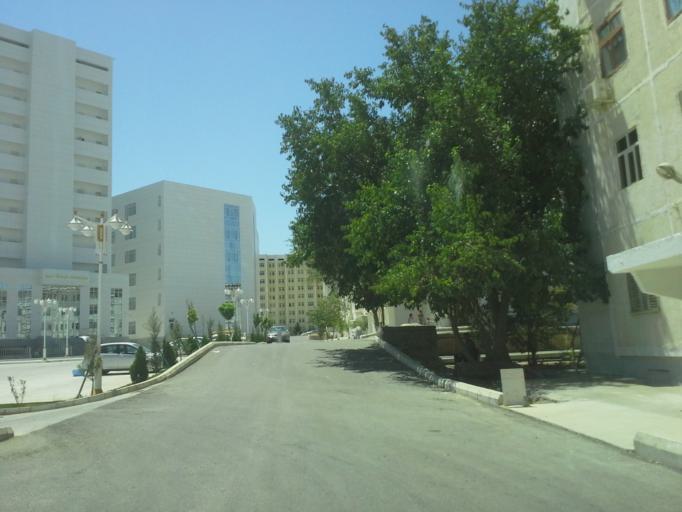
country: TM
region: Ahal
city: Ashgabat
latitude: 37.9121
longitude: 58.3965
